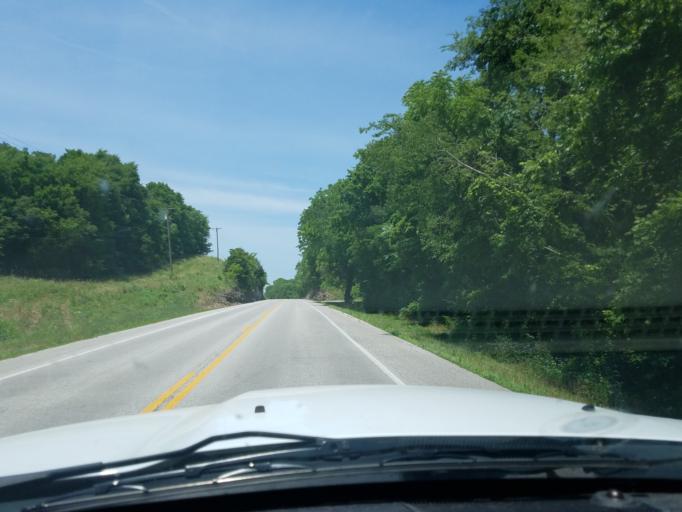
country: US
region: Tennessee
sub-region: Trousdale County
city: Hartsville
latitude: 36.4236
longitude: -86.2666
